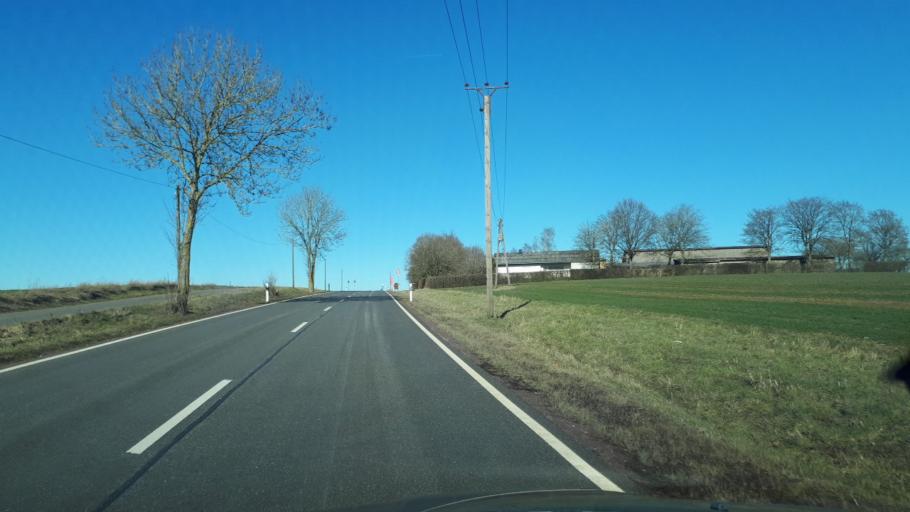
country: DE
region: Rheinland-Pfalz
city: Strotzbusch
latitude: 50.1037
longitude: 6.9651
